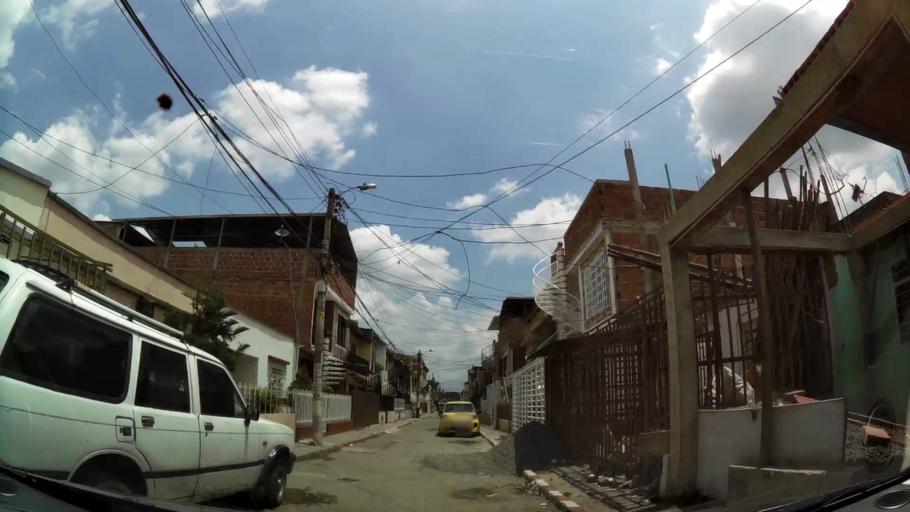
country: CO
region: Valle del Cauca
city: Cali
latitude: 3.4530
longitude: -76.4821
